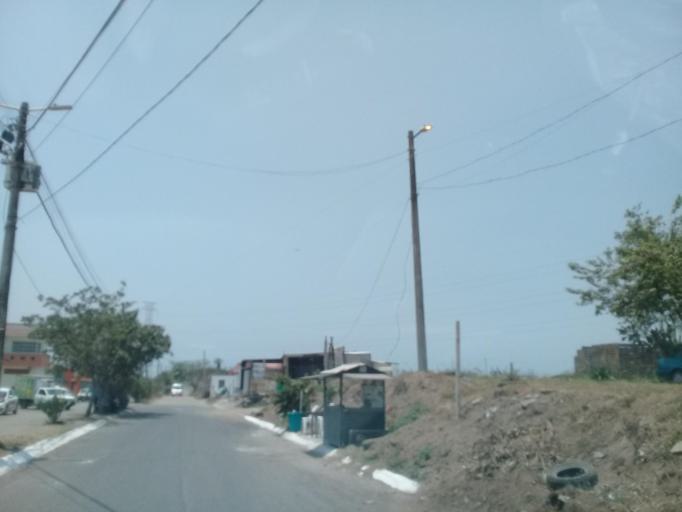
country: MX
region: Veracruz
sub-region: Veracruz
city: Las Amapolas
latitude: 19.1561
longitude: -96.2146
